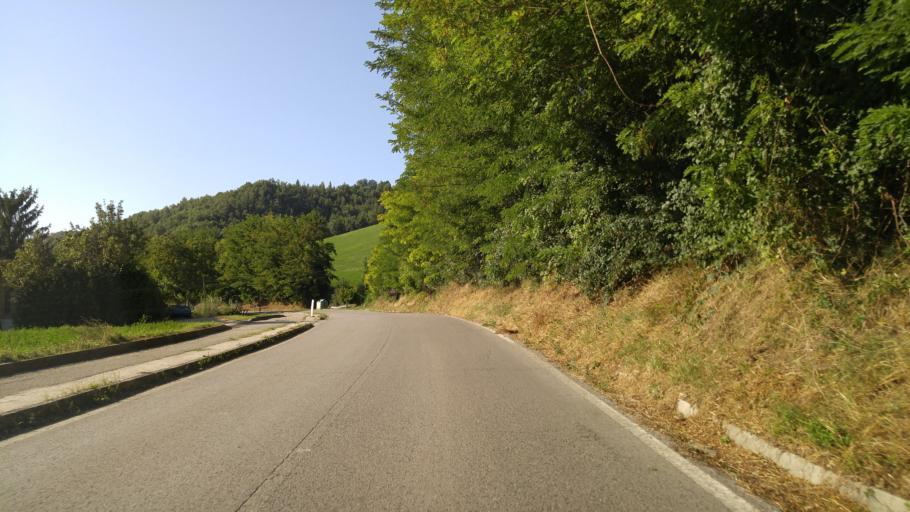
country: IT
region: The Marches
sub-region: Provincia di Pesaro e Urbino
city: Urbania
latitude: 43.6804
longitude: 12.5206
